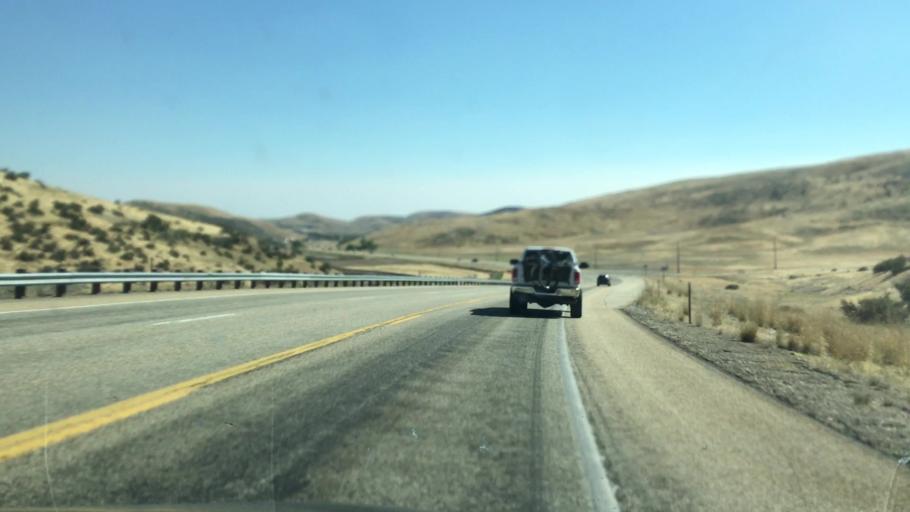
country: US
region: Idaho
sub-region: Ada County
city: Eagle
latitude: 43.8023
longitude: -116.2644
